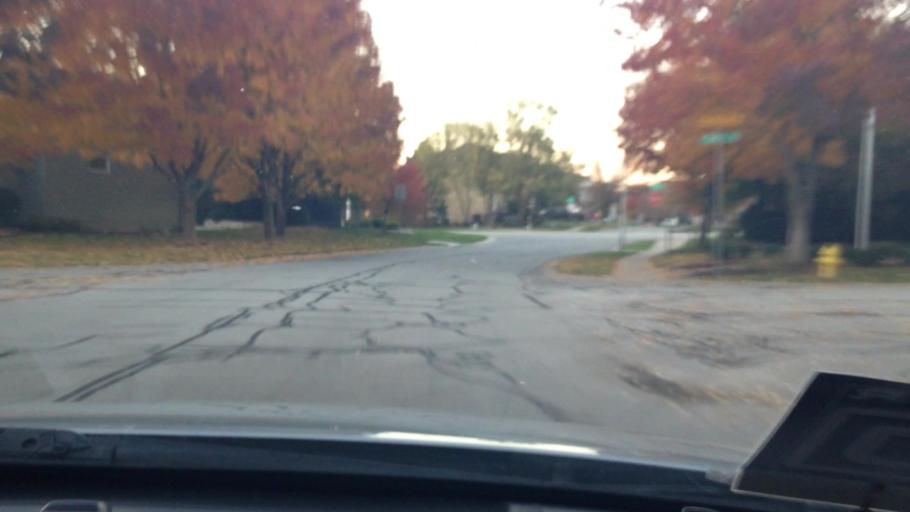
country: US
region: Kansas
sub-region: Johnson County
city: Lenexa
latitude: 38.8684
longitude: -94.7207
